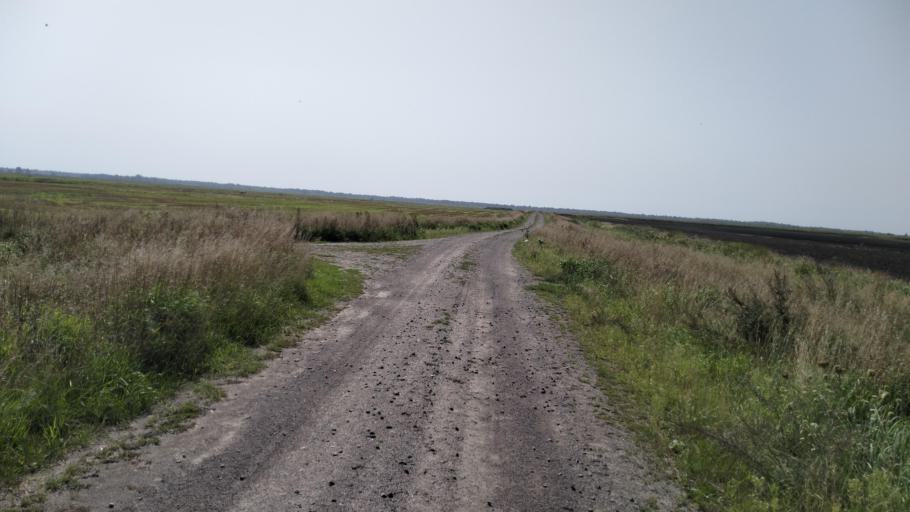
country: BY
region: Brest
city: Davyd-Haradok
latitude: 51.9969
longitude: 27.1650
